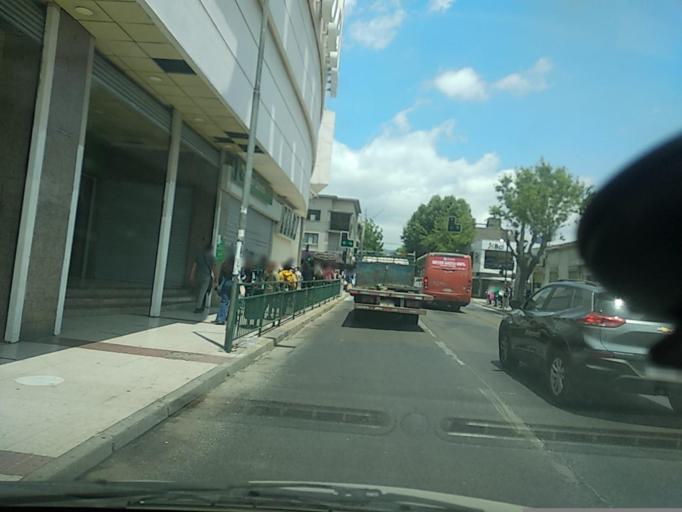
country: CL
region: Valparaiso
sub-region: Provincia de Marga Marga
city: Quilpue
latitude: -33.0466
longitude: -71.4416
